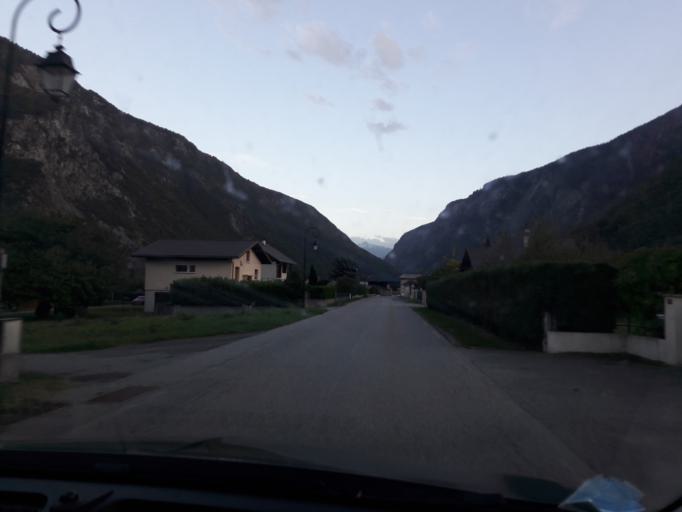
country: FR
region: Rhone-Alpes
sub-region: Departement de la Savoie
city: La Chambre
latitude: 45.3417
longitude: 6.3008
